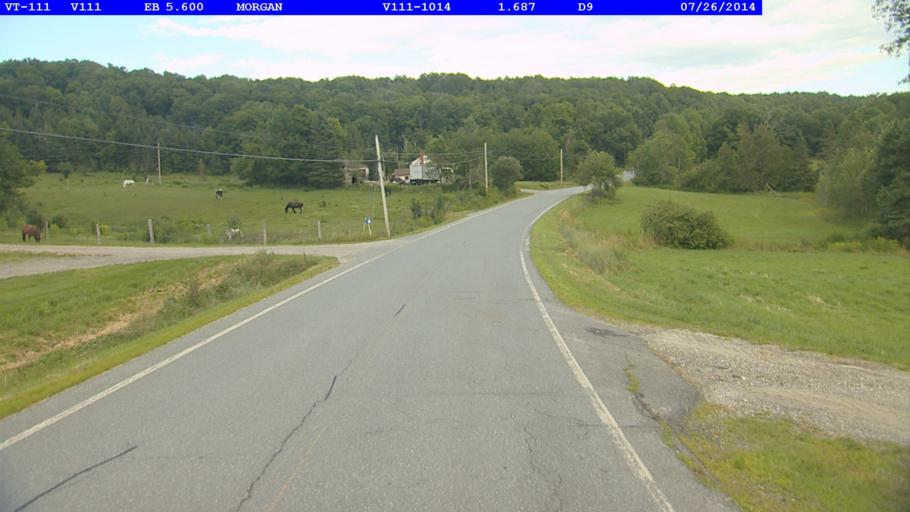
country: US
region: Vermont
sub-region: Orleans County
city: Newport
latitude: 44.9223
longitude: -72.0335
